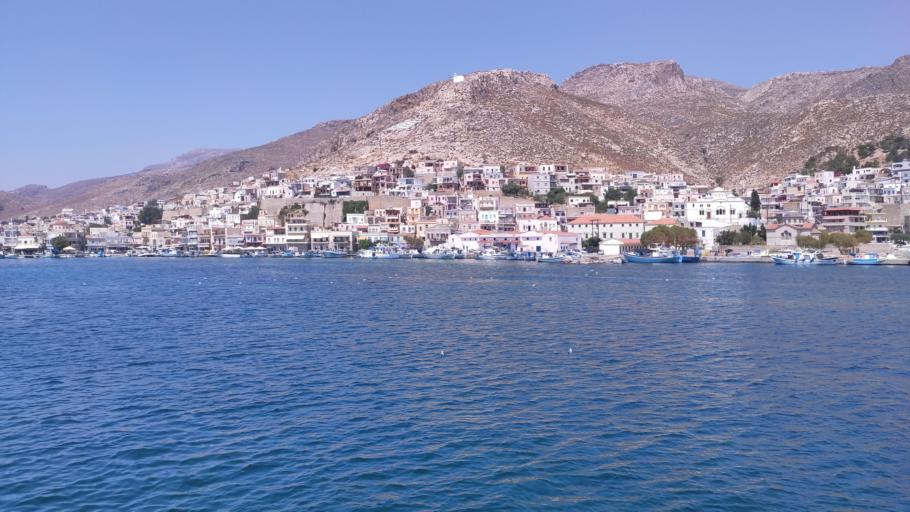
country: GR
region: South Aegean
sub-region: Nomos Dodekanisou
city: Kalymnos
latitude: 36.9491
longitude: 26.9895
